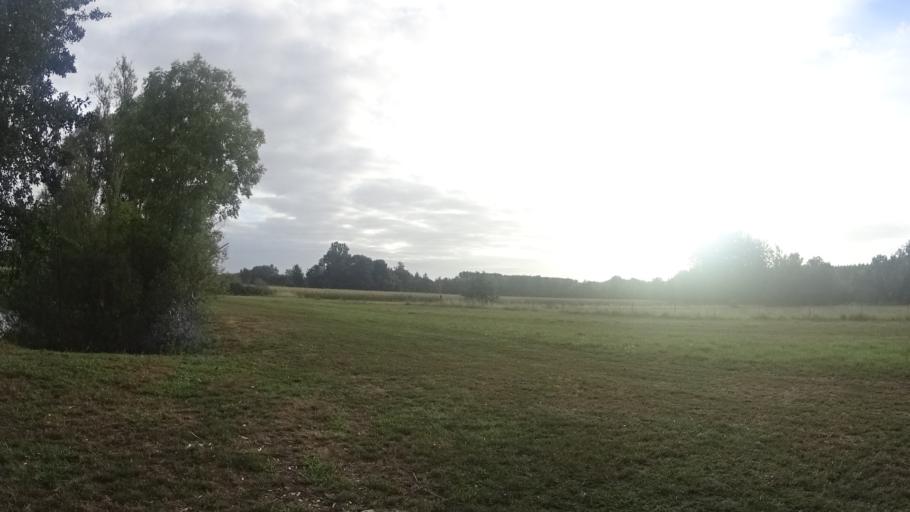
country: FR
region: Picardie
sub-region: Departement de l'Aisne
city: Ribemont
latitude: 49.8229
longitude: 3.4622
